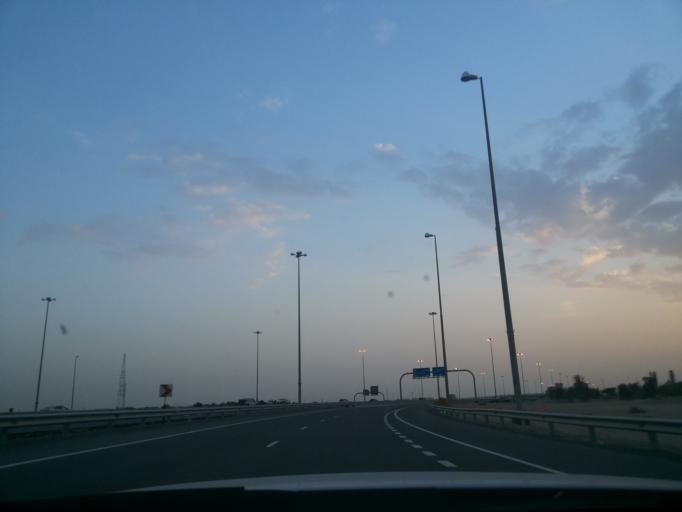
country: AE
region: Abu Dhabi
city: Abu Dhabi
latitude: 24.6921
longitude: 54.7765
